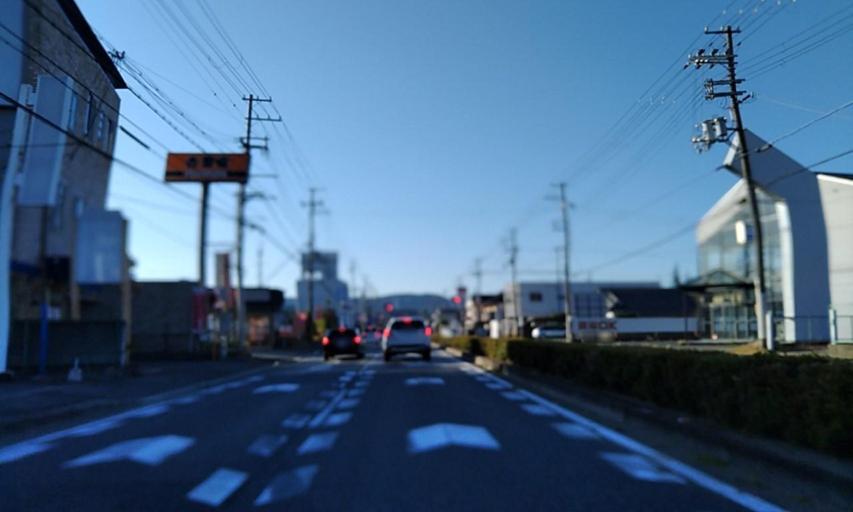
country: JP
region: Wakayama
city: Kainan
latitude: 34.1787
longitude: 135.1863
